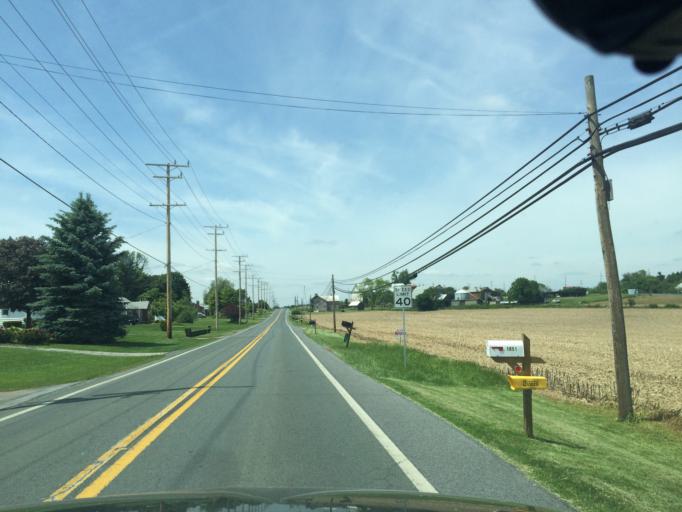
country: US
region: Maryland
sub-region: Carroll County
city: Westminster
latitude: 39.5333
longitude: -76.9309
